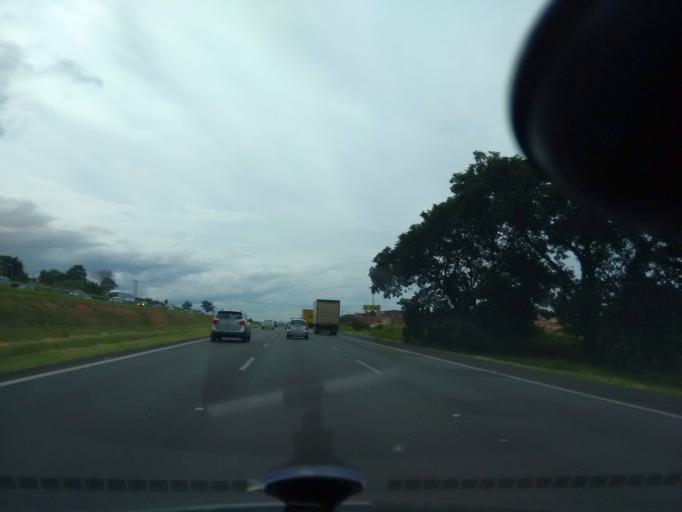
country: BR
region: Sao Paulo
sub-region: Campinas
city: Campinas
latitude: -22.9368
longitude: -47.1267
